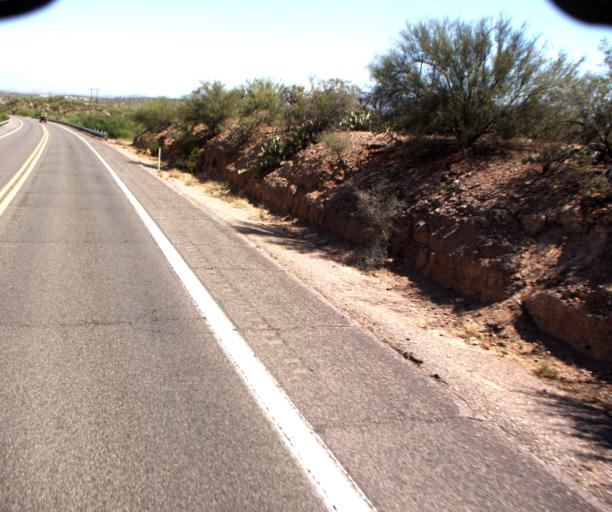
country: US
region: Arizona
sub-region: Pinal County
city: Mammoth
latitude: 32.8560
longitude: -110.7084
